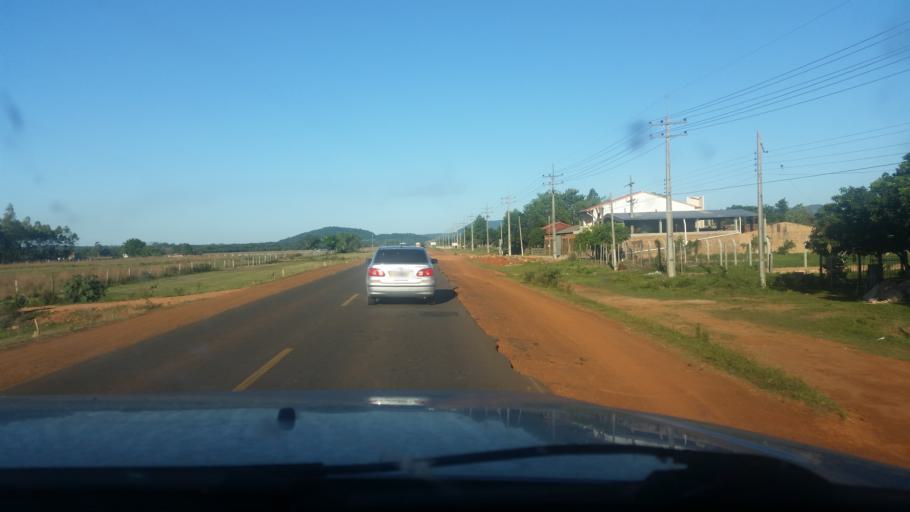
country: PY
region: Guaira
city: Mbocayaty
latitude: -25.7182
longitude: -56.4002
